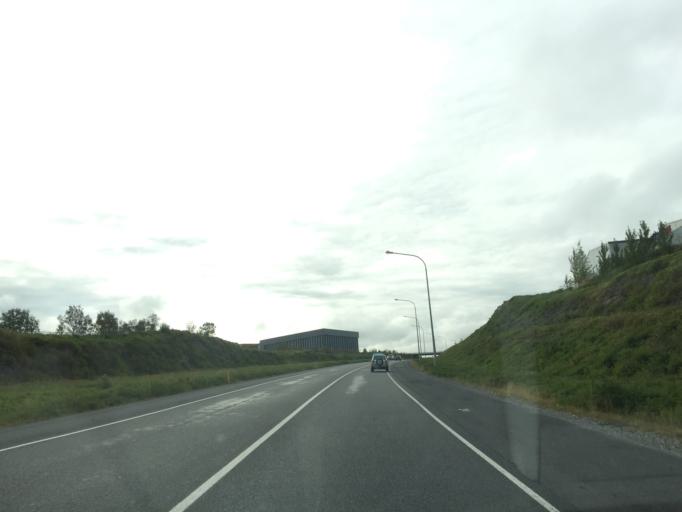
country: IS
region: Capital Region
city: Mosfellsbaer
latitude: 64.1188
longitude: -21.7818
